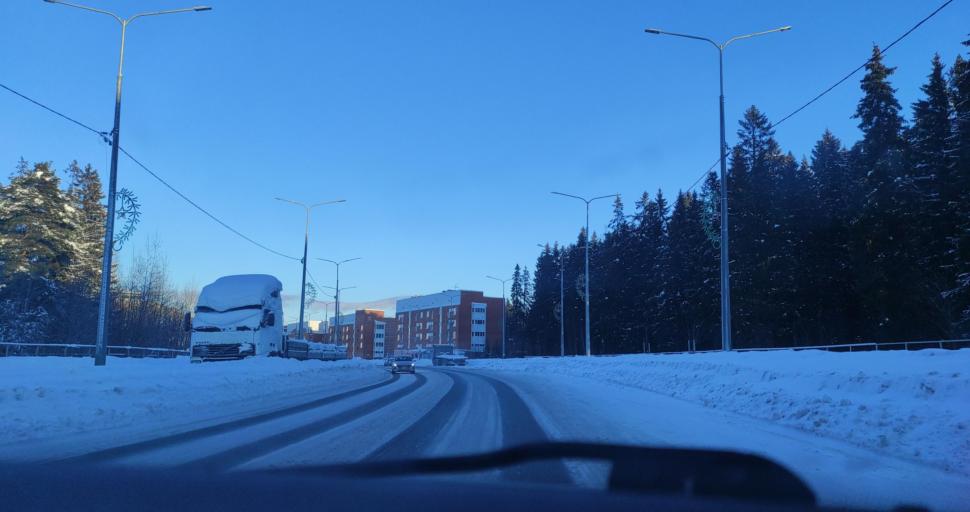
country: RU
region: Republic of Karelia
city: Petrozavodsk
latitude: 61.7755
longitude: 34.3208
